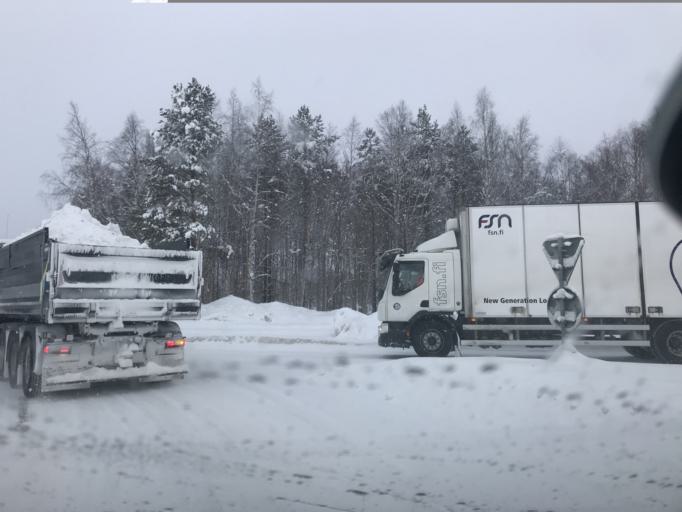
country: SE
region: Norrbotten
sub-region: Lulea Kommun
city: Lulea
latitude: 65.6127
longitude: 22.1348
